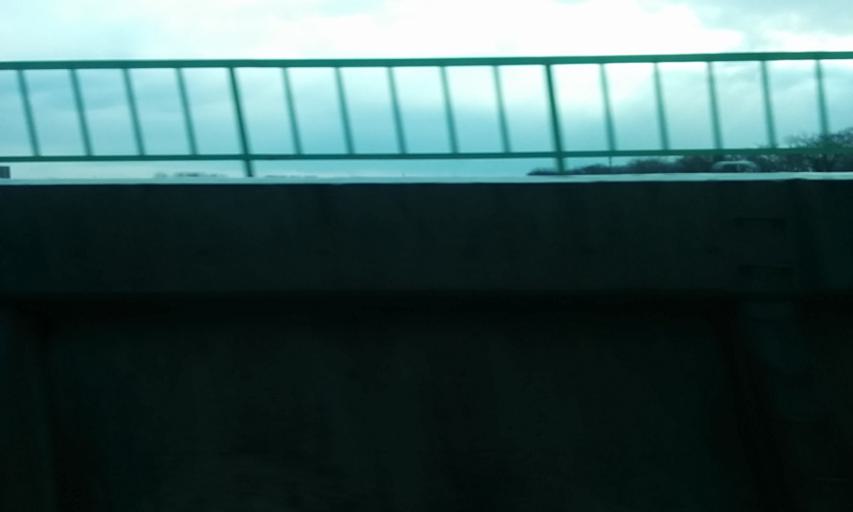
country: JP
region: Saitama
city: Kawaguchi
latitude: 35.7889
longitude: 139.7173
